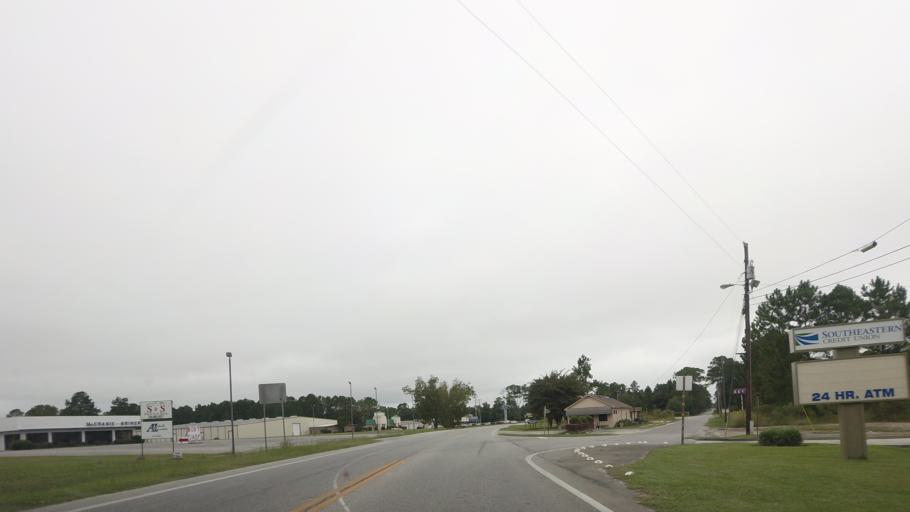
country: US
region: Georgia
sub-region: Berrien County
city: Nashville
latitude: 31.1933
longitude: -83.2508
